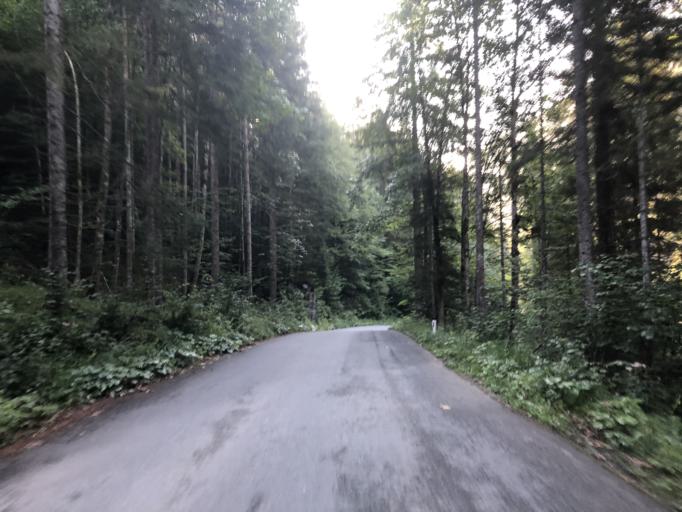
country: AT
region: Tyrol
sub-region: Politischer Bezirk Kitzbuhel
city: Schwendt
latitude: 47.5799
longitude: 12.3714
